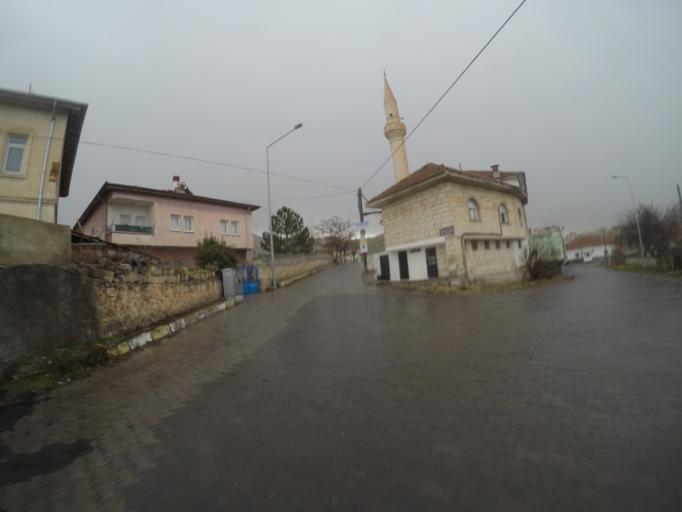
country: TR
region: Nevsehir
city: Goereme
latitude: 38.6702
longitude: 34.8400
